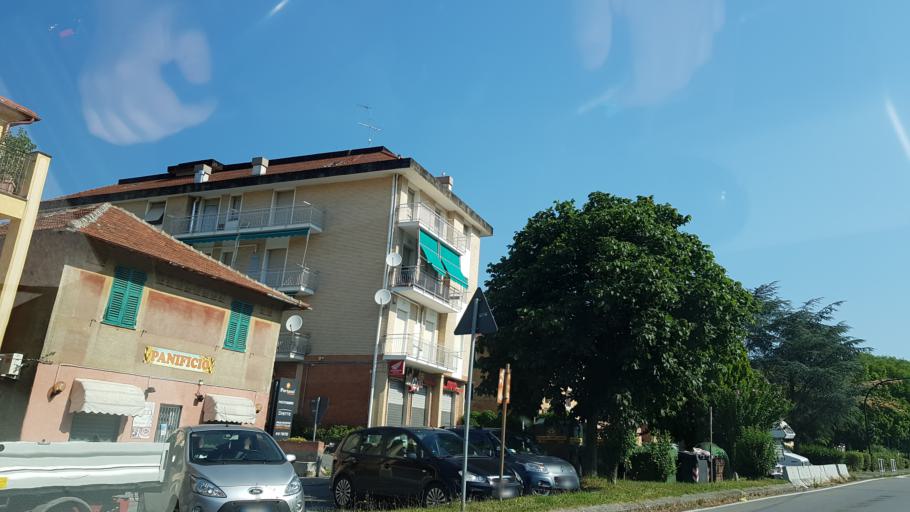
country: IT
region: Liguria
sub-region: Provincia di Genova
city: Pedemonte
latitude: 44.4966
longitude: 8.9211
